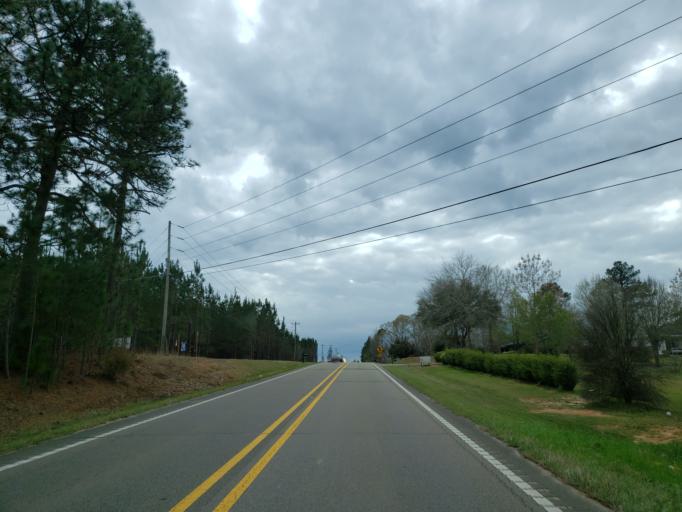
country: US
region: Mississippi
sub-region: Lamar County
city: Purvis
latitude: 31.2094
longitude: -89.3630
